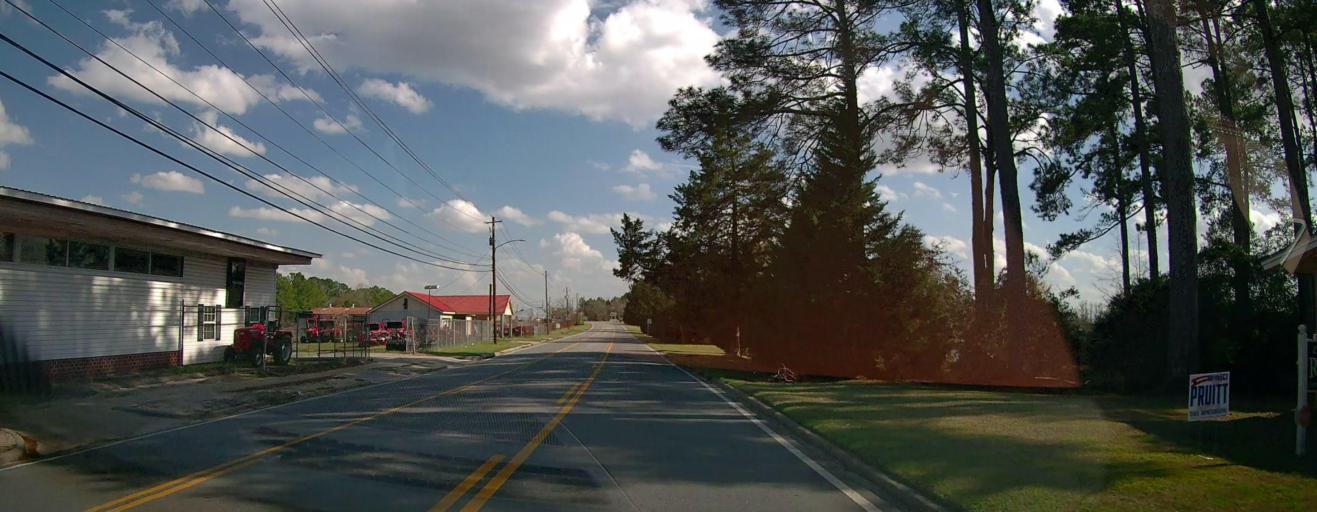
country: US
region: Georgia
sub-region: Dodge County
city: Eastman
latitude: 32.1858
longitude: -83.1712
